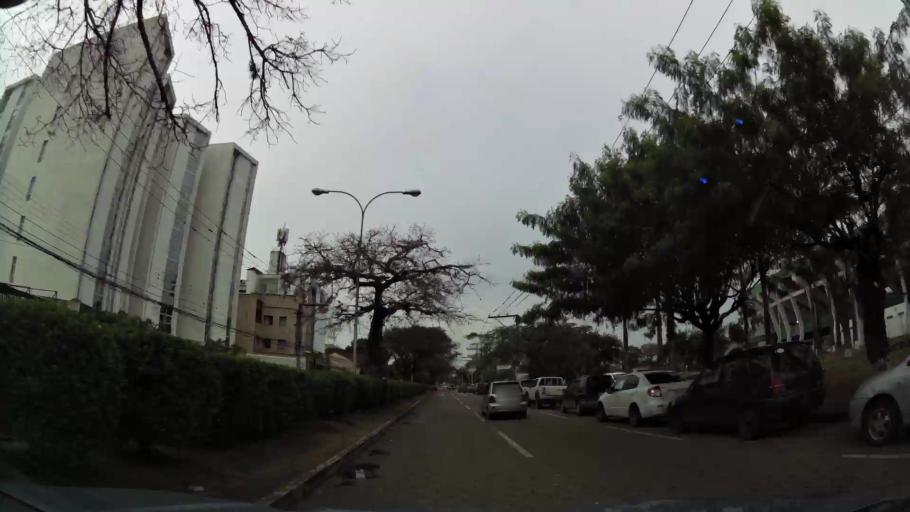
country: BO
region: Santa Cruz
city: Santa Cruz de la Sierra
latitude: -17.7956
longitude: -63.1823
